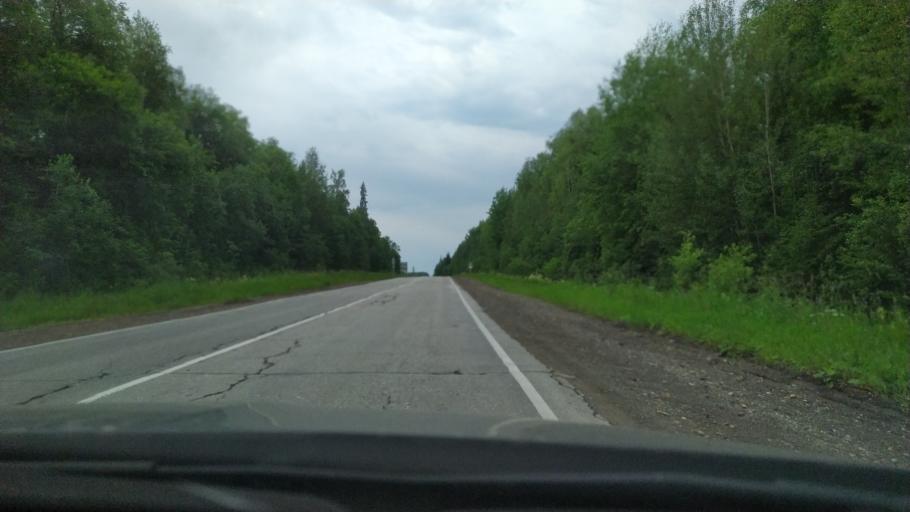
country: RU
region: Perm
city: Gremyachinsk
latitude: 58.4295
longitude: 57.8838
